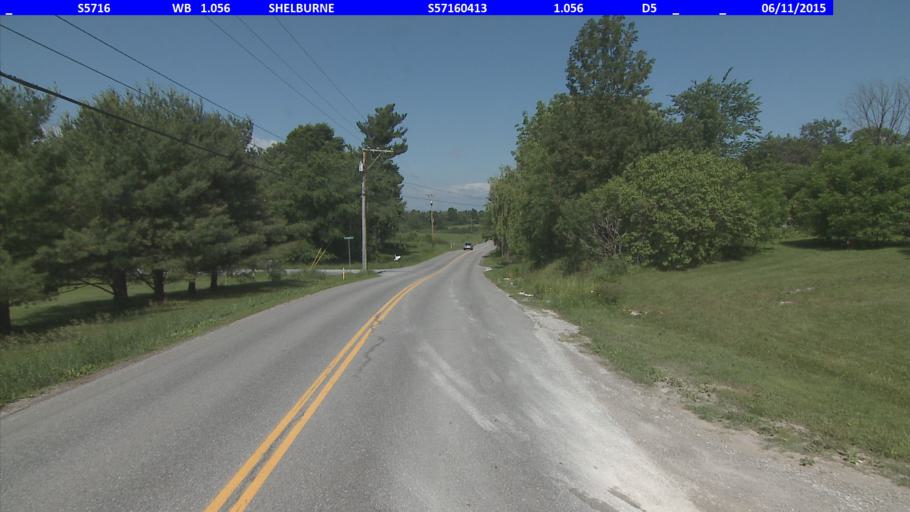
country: US
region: Vermont
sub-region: Chittenden County
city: Hinesburg
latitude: 44.3716
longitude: -73.1913
